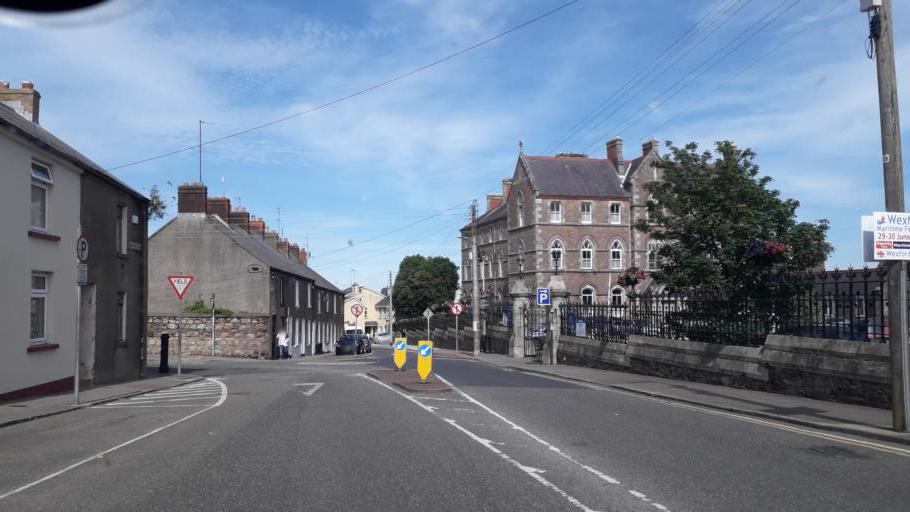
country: IE
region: Leinster
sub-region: Loch Garman
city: Loch Garman
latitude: 52.3347
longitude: -6.4621
